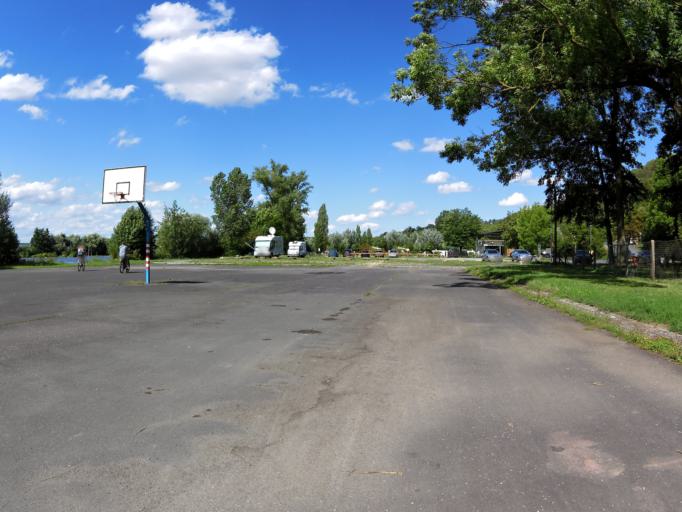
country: DE
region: Bavaria
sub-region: Regierungsbezirk Unterfranken
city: Segnitz
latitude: 49.6709
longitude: 10.1485
